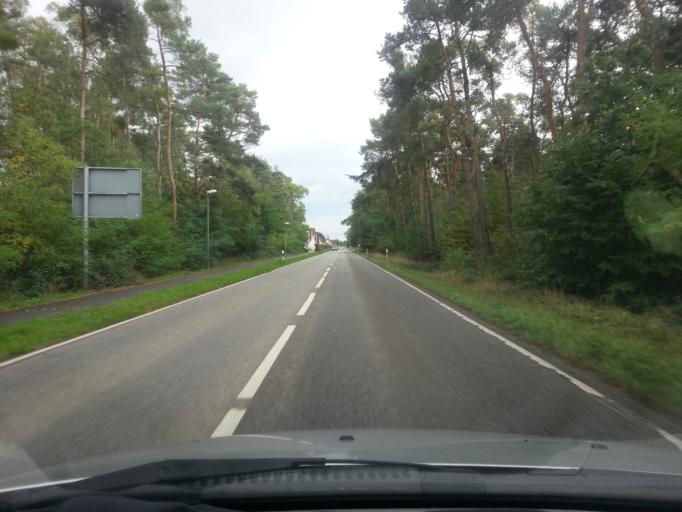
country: DE
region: Rheinland-Pfalz
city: Birkenheide
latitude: 49.4799
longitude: 8.2762
